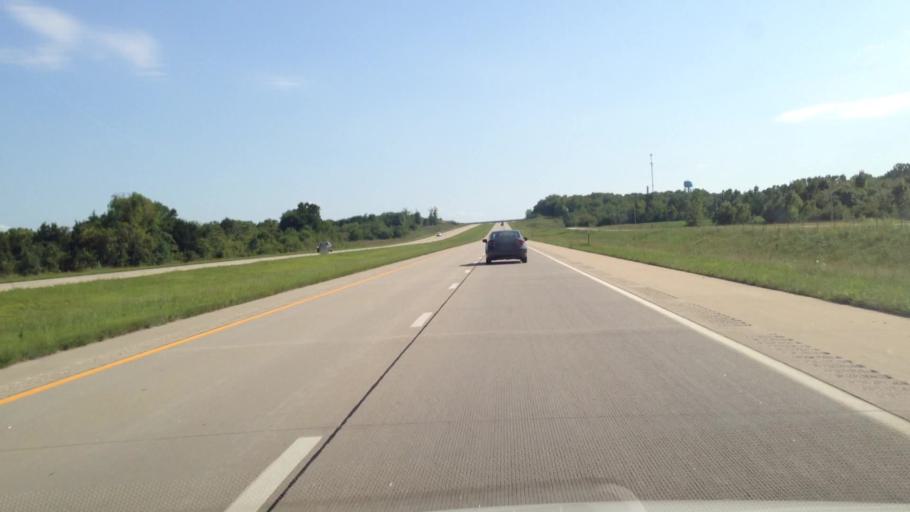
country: US
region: Kansas
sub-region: Linn County
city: Pleasanton
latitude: 38.1256
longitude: -94.7147
